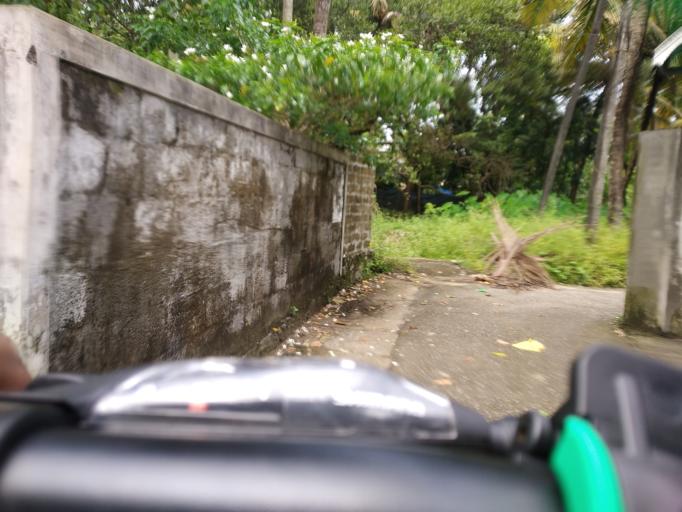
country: IN
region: Kerala
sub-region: Ernakulam
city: Elur
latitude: 10.0765
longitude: 76.2153
